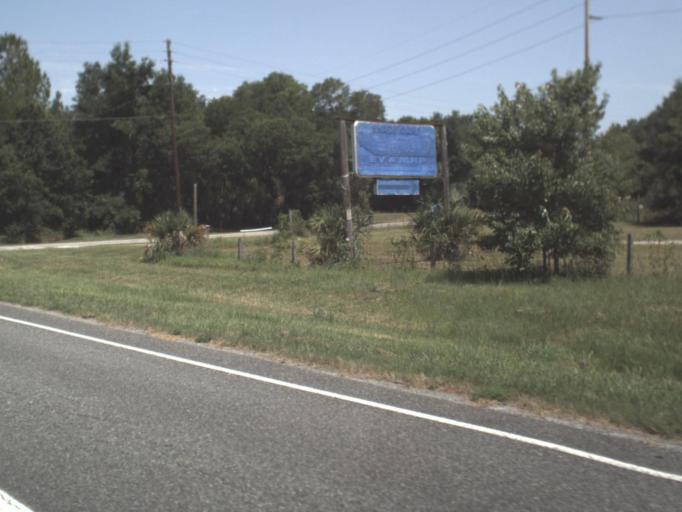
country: US
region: Florida
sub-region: Dixie County
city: Cross City
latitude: 29.6101
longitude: -83.0837
